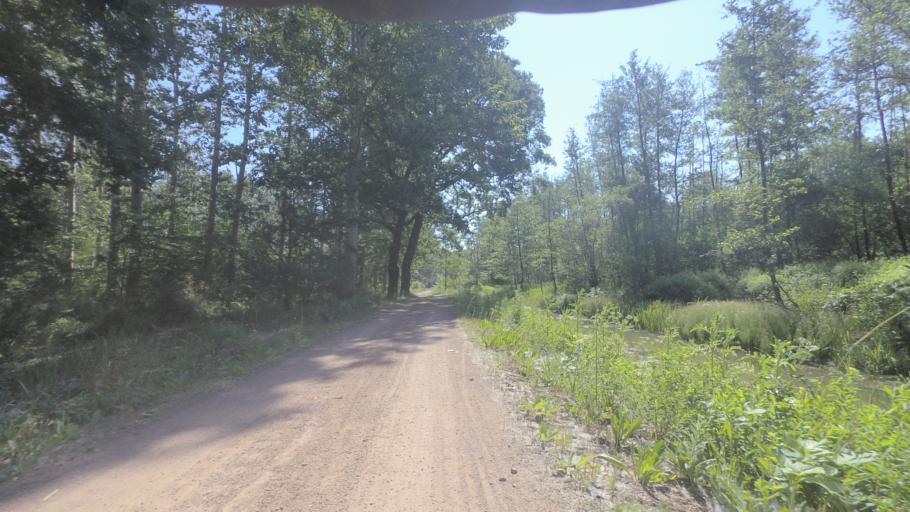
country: DE
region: Saxony-Anhalt
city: Vockerode
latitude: 51.8258
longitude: 12.3528
